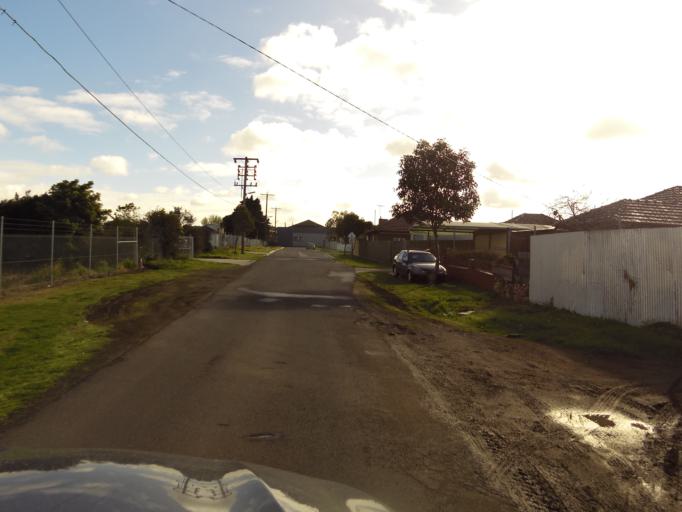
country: AU
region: Victoria
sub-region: Maribyrnong
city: Kingsville
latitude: -37.8049
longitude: 144.8665
